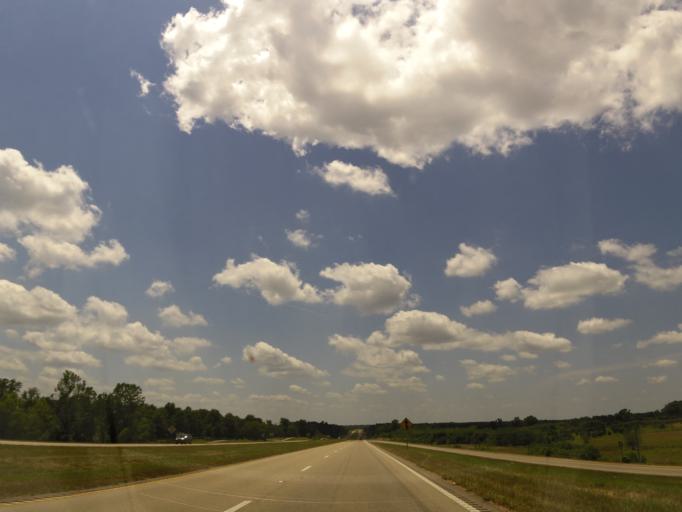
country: US
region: Mississippi
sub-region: Pontotoc County
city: Pontotoc
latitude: 34.2866
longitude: -89.0277
